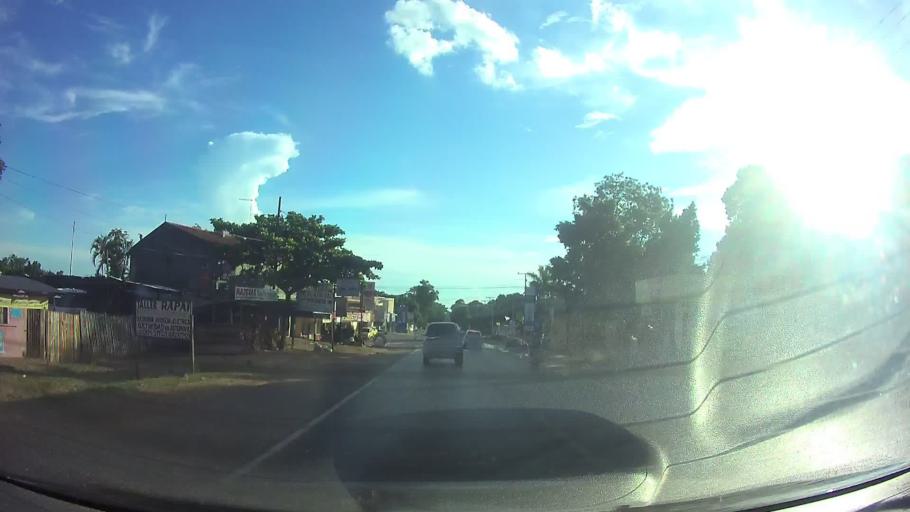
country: PY
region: Central
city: Lambare
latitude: -25.3509
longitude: -57.5917
